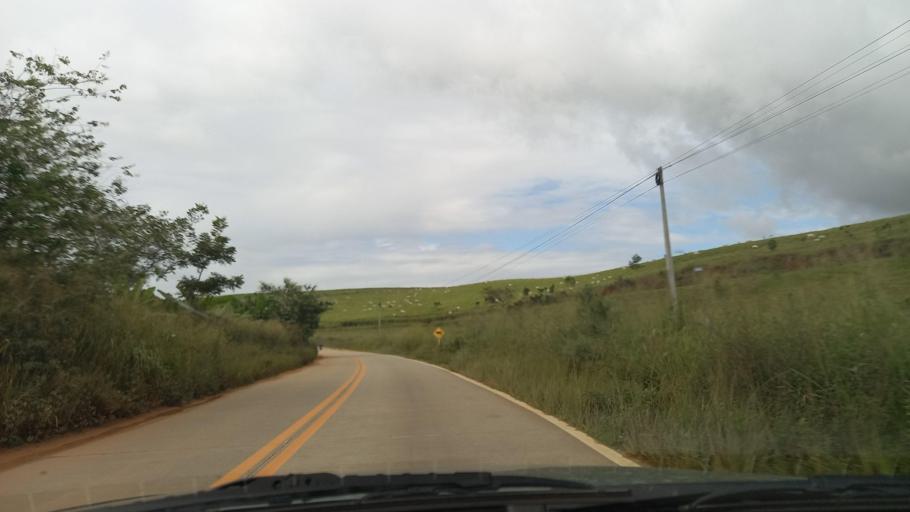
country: BR
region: Pernambuco
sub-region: Maraial
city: Maraial
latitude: -8.7588
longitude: -35.8507
